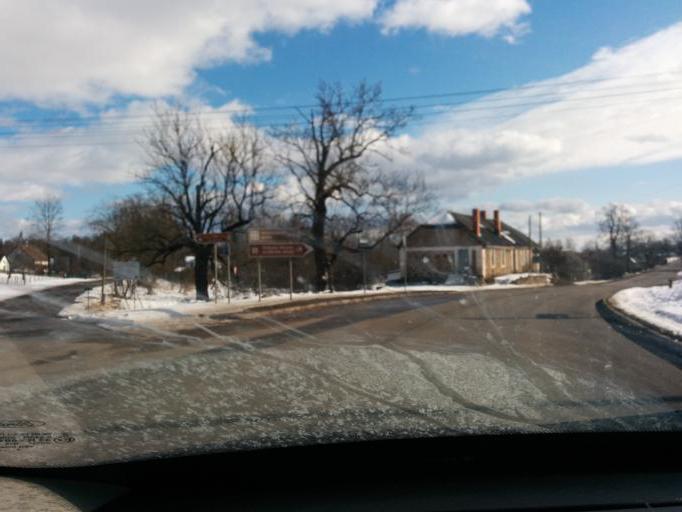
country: LV
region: Gulbenes Rajons
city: Gulbene
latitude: 57.1842
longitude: 26.7363
